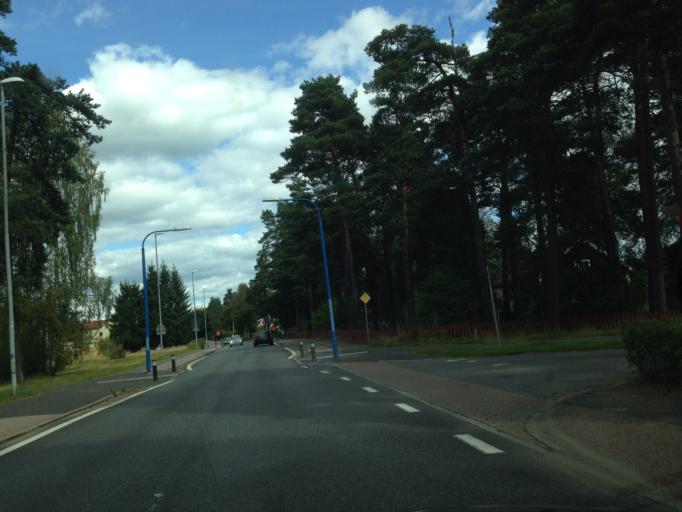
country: SE
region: Joenkoeping
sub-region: Vaggeryds Kommun
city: Vaggeryd
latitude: 57.4926
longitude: 14.1300
